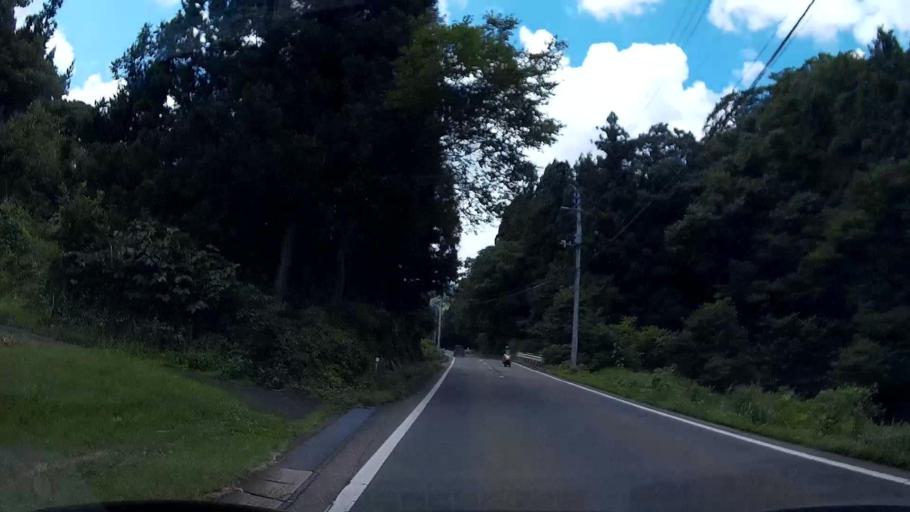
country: JP
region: Niigata
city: Shiozawa
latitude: 37.0195
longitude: 138.8174
